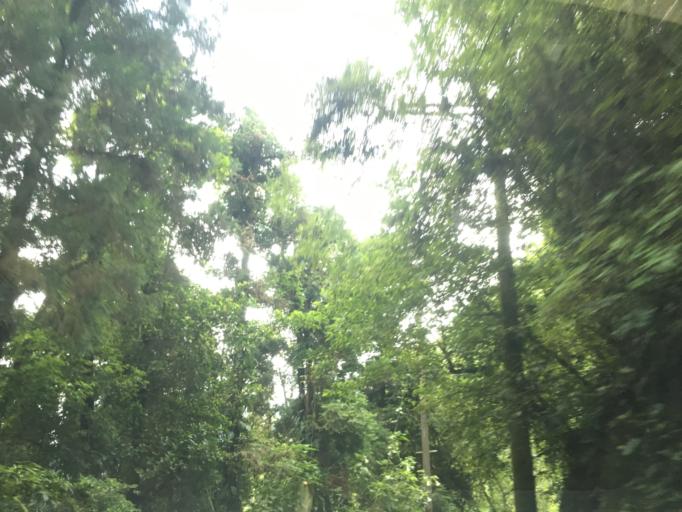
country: TW
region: Taiwan
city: Lugu
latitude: 23.5428
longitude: 120.7082
